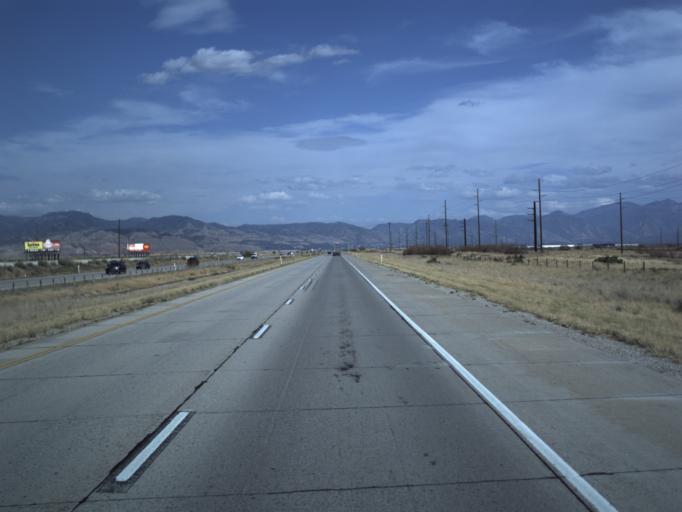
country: US
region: Utah
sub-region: Salt Lake County
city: Magna
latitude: 40.7707
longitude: -112.1054
